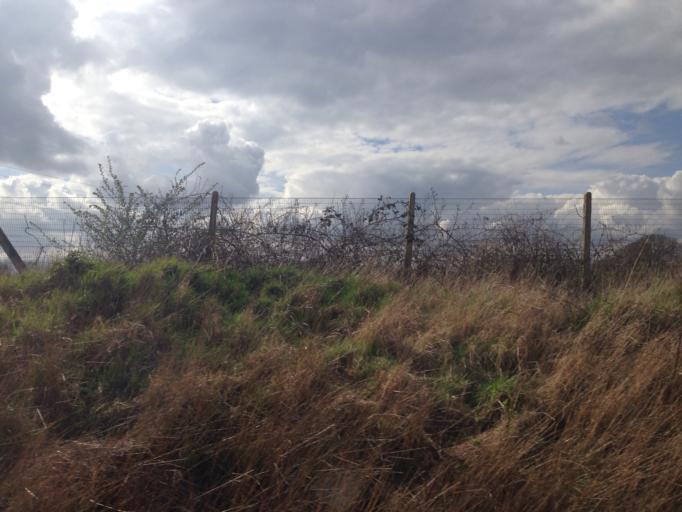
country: GB
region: England
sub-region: Greater London
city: Mitcham
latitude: 51.3884
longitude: -0.1527
